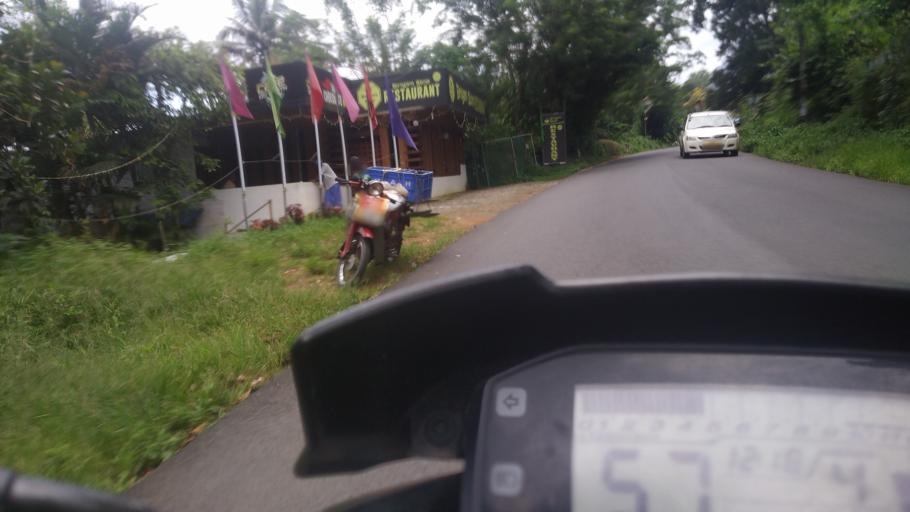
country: IN
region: Kerala
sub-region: Idukki
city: Munnar
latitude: 10.0193
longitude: 77.0049
